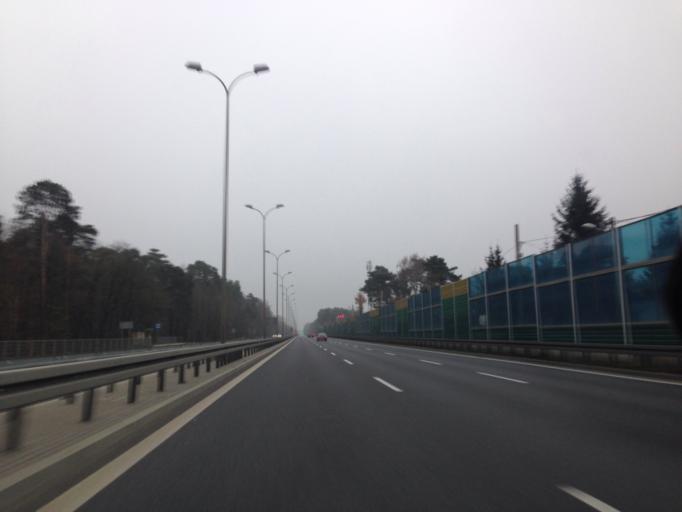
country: PL
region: Lodz Voivodeship
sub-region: Powiat lodzki wschodni
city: Tuszyn
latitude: 51.6226
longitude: 19.5161
